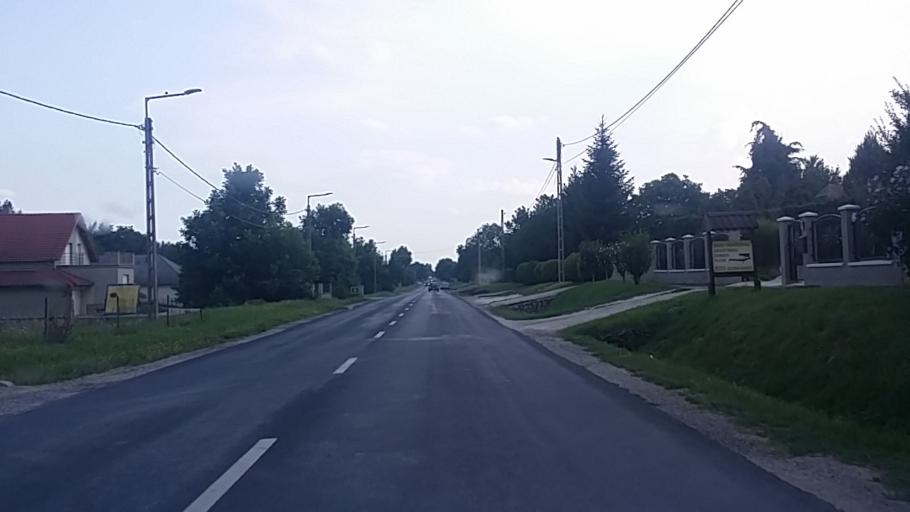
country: HU
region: Zala
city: Heviz
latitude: 46.7546
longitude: 17.1750
